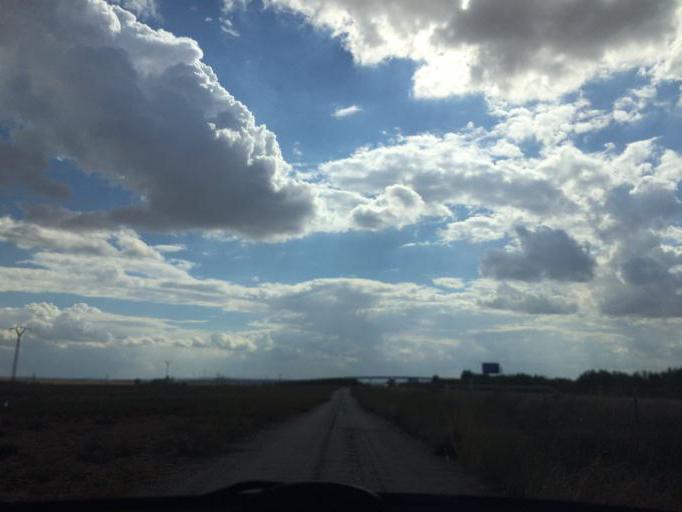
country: ES
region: Castille-La Mancha
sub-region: Provincia de Albacete
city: Albacete
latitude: 38.9511
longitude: -1.8246
